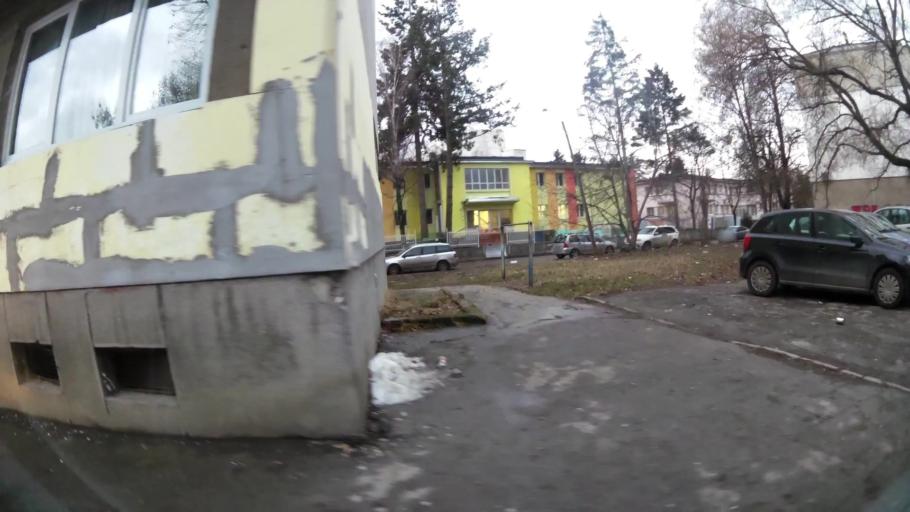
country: BG
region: Sofia-Capital
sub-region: Stolichna Obshtina
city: Sofia
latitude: 42.7356
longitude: 23.3034
